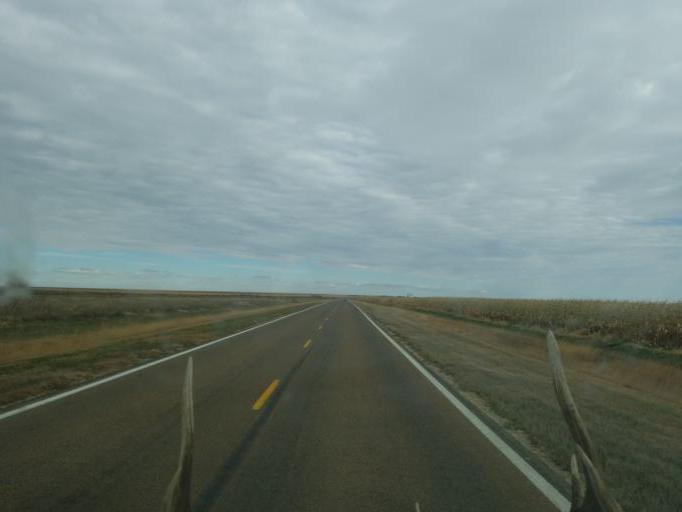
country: US
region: Kansas
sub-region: Logan County
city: Oakley
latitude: 39.0684
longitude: -101.2187
